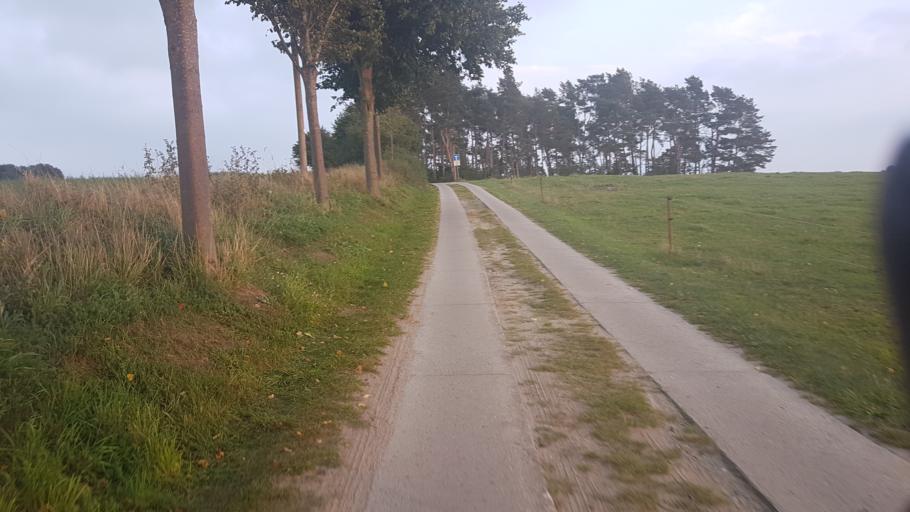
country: DE
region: Mecklenburg-Vorpommern
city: Putbus
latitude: 54.3504
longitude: 13.5306
